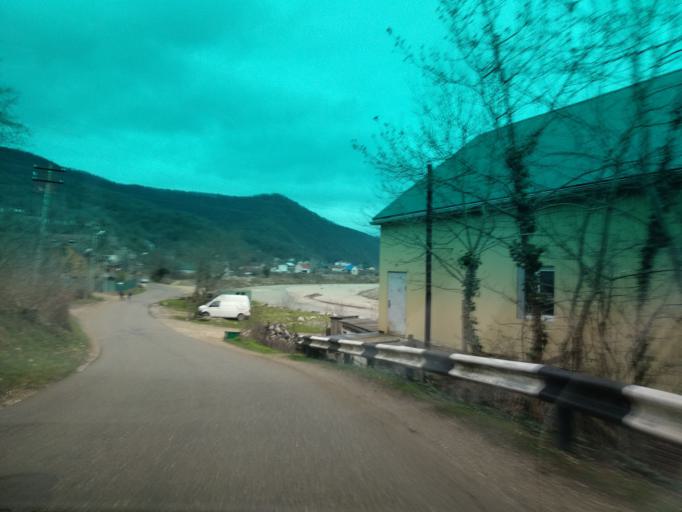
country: RU
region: Krasnodarskiy
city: Novomikhaylovskiy
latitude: 44.2565
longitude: 38.8511
